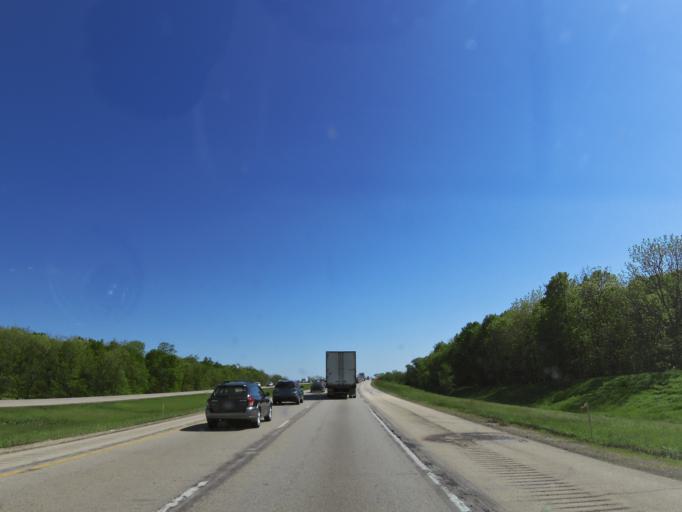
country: US
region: Illinois
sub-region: Ogle County
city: Davis Junction
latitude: 42.0545
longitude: -89.0194
